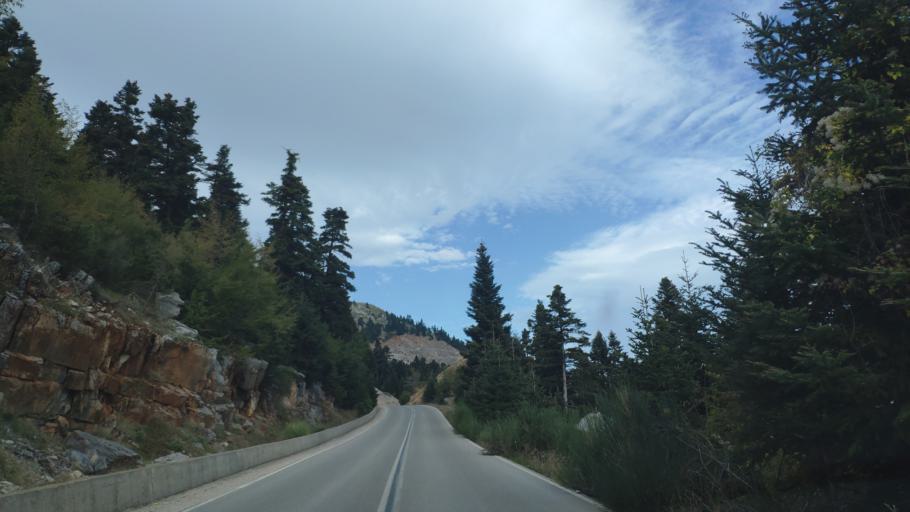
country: GR
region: Central Greece
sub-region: Nomos Fokidos
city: Amfissa
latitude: 38.6475
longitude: 22.3862
